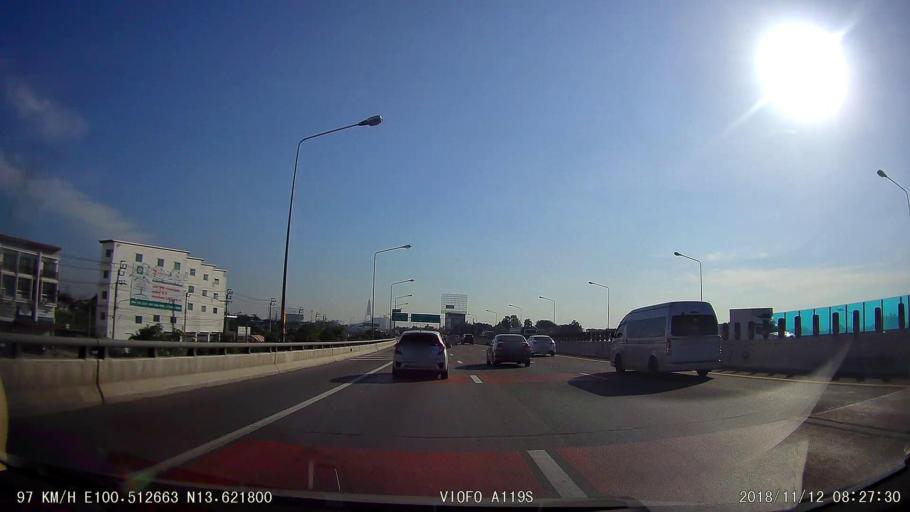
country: TH
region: Bangkok
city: Thung Khru
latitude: 13.6219
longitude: 100.5130
